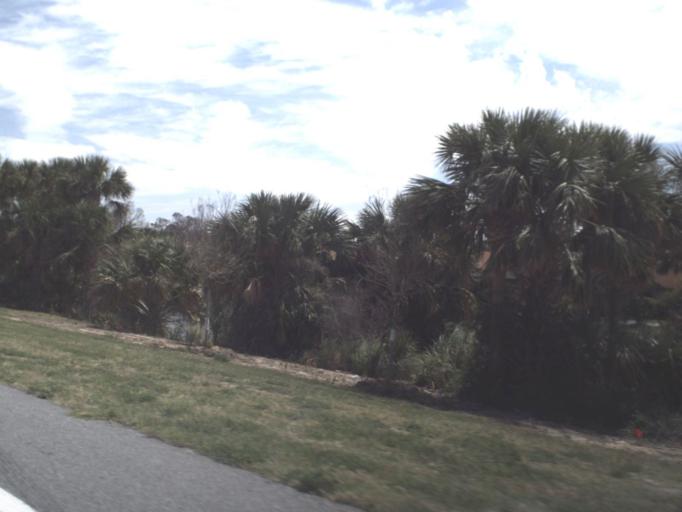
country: US
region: Florida
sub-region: Flagler County
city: Palm Coast
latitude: 29.6476
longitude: -81.2066
